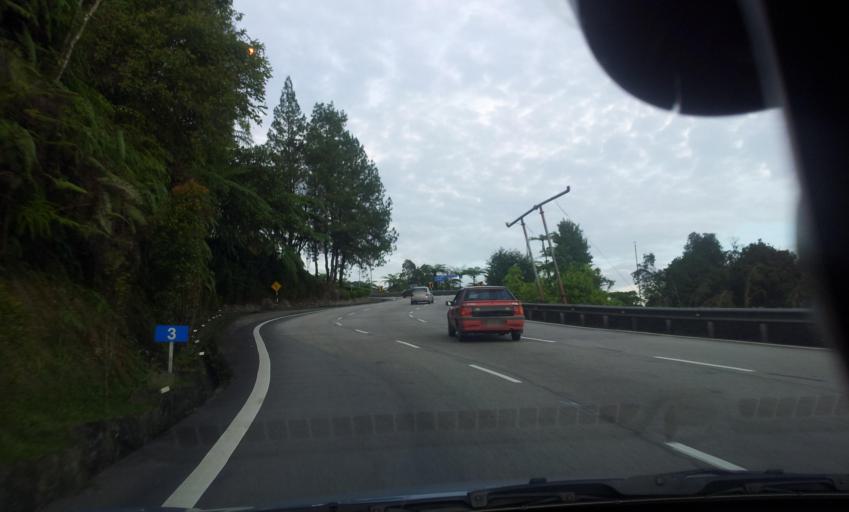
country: MY
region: Pahang
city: Kampung Bukit Tinggi, Bentong
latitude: 3.4122
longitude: 101.7865
